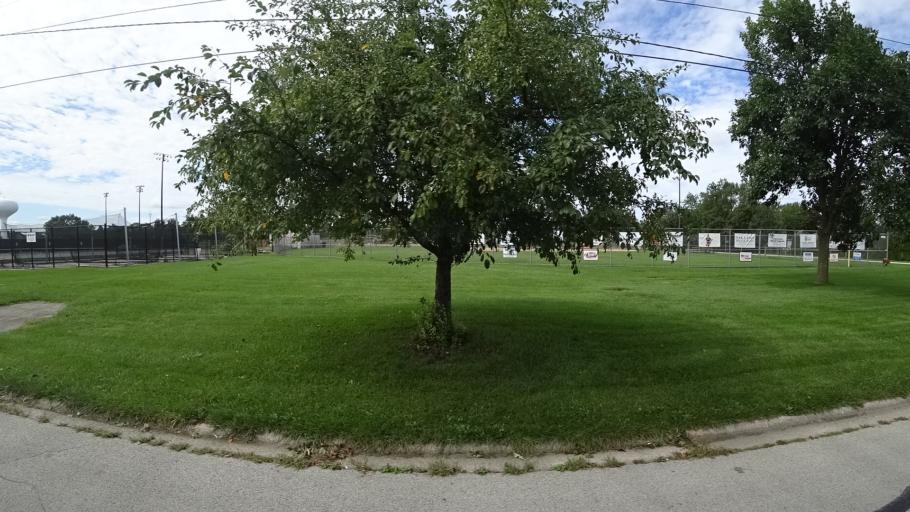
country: US
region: Illinois
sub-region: Cook County
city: Burbank
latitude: 41.7227
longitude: -87.7898
